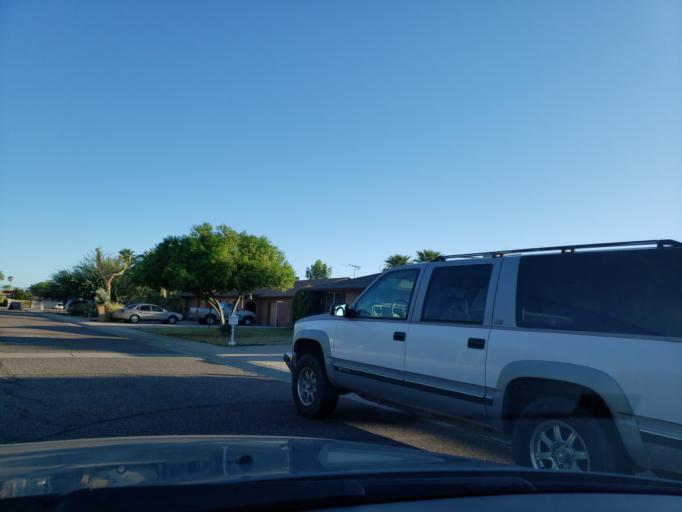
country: US
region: Arizona
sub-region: Maricopa County
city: Paradise Valley
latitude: 33.5843
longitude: -112.0057
